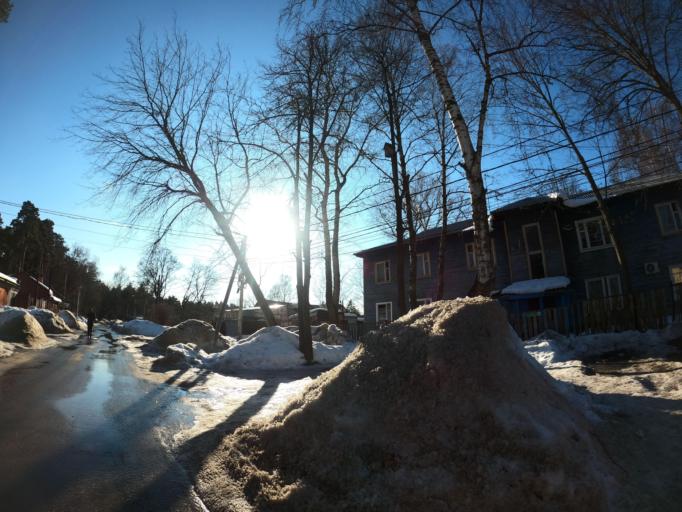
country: RU
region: Moskovskaya
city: Kraskovo
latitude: 55.6418
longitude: 37.9938
